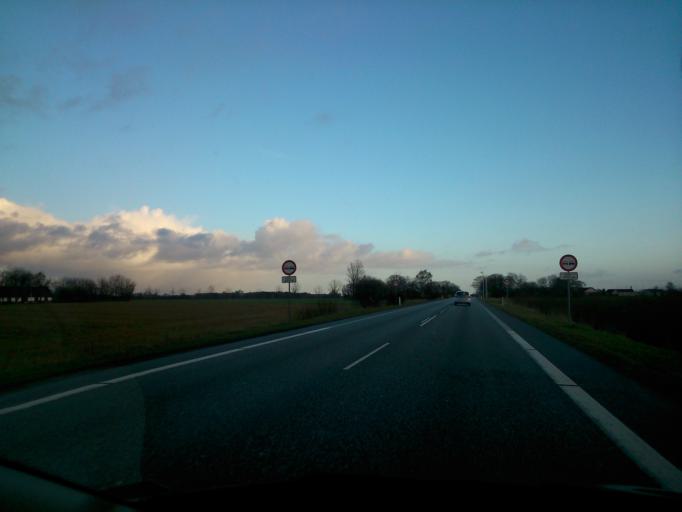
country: DK
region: Central Jutland
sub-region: Herning Kommune
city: Snejbjerg
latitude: 56.1260
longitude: 8.8497
